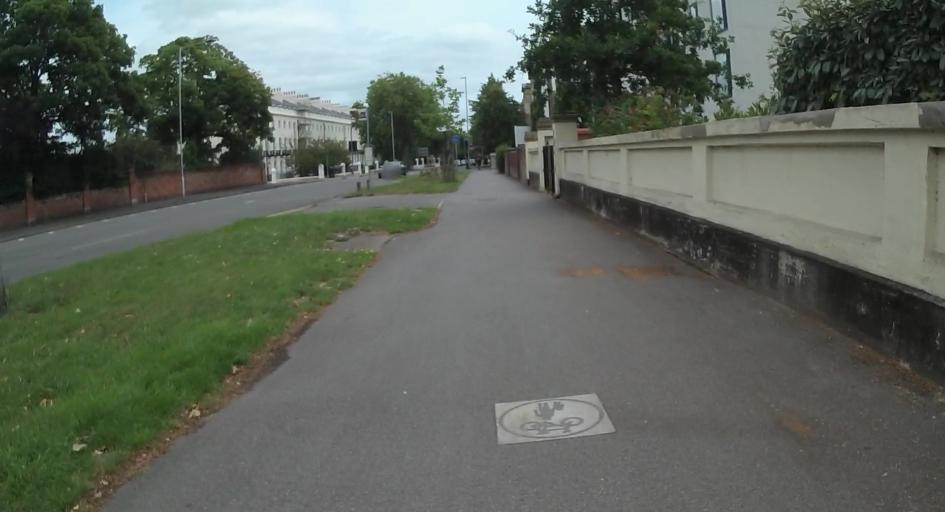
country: GB
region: England
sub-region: Reading
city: Reading
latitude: 51.4508
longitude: -0.9641
